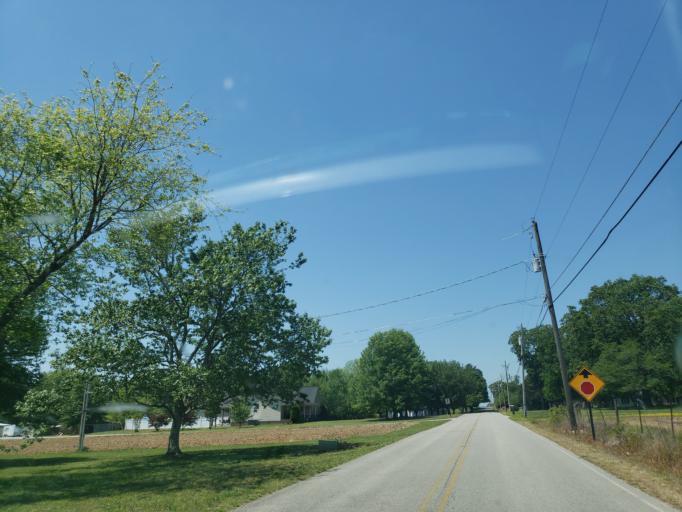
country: US
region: Alabama
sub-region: Madison County
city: Hazel Green
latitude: 34.9620
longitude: -86.6395
